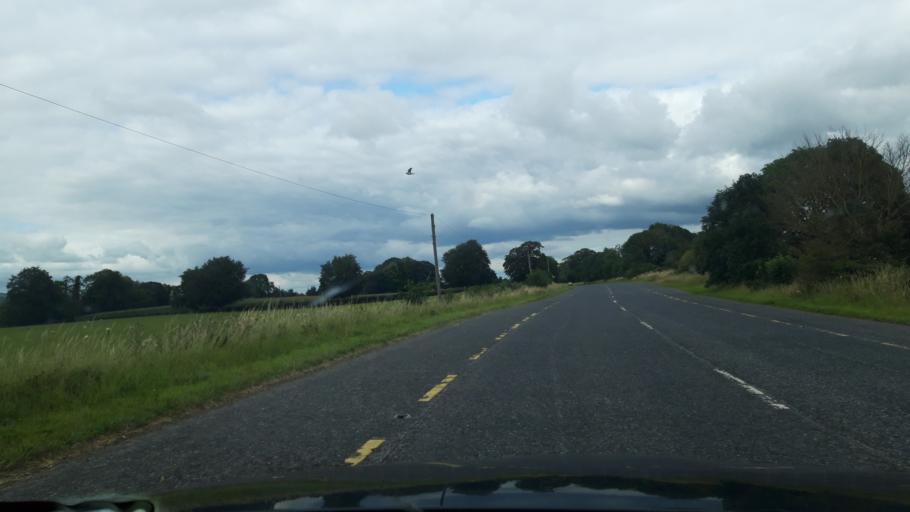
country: IE
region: Leinster
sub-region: County Carlow
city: Bagenalstown
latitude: 52.6530
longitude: -7.0444
